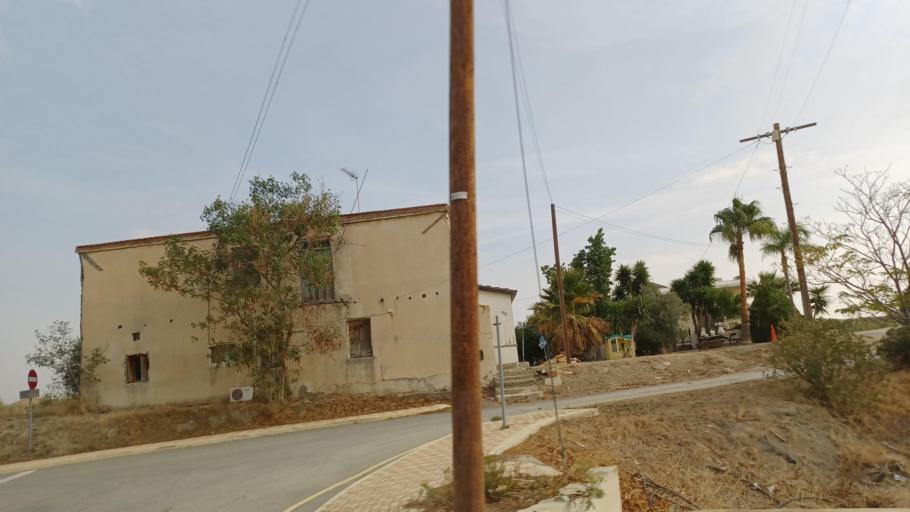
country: CY
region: Larnaka
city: Troulloi
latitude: 35.0083
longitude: 33.5705
